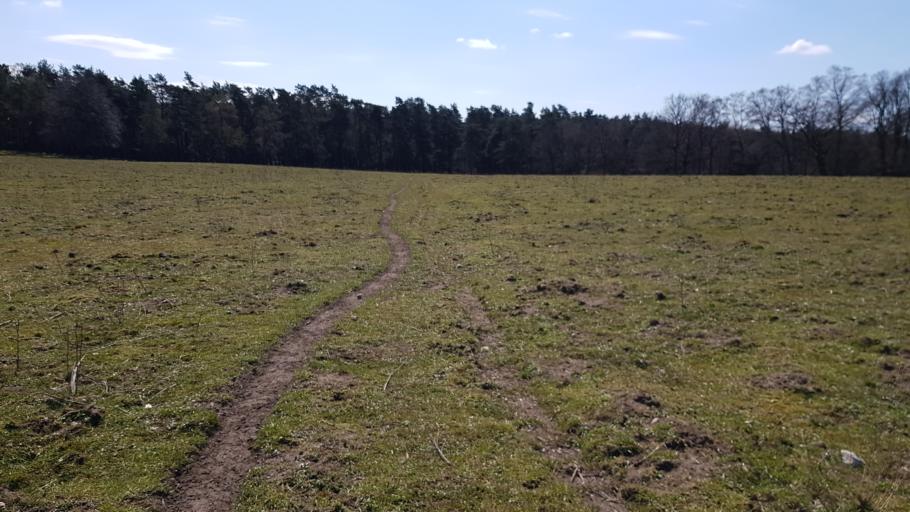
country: NL
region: Gelderland
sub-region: Gemeente Rozendaal
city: Rozendaal
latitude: 52.0751
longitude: 5.9561
